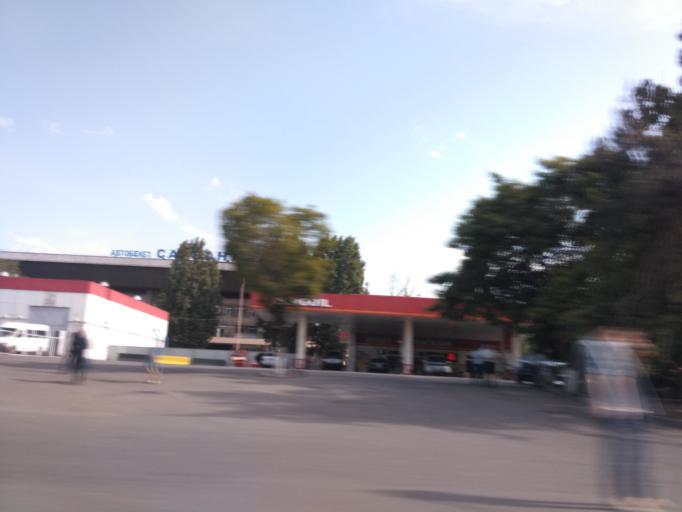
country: KZ
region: Almaty Qalasy
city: Almaty
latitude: 43.2459
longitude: 76.8569
